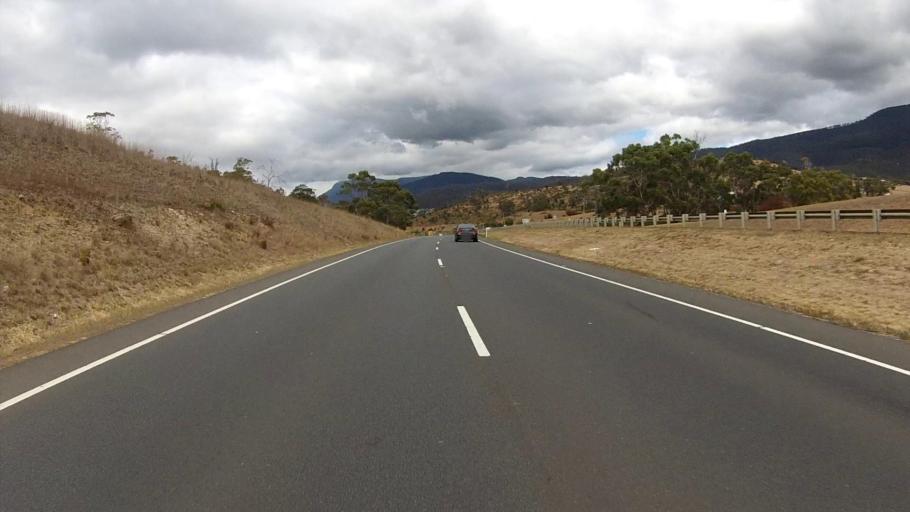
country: AU
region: Tasmania
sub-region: Glenorchy
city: Claremont
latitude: -42.7752
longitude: 147.2391
